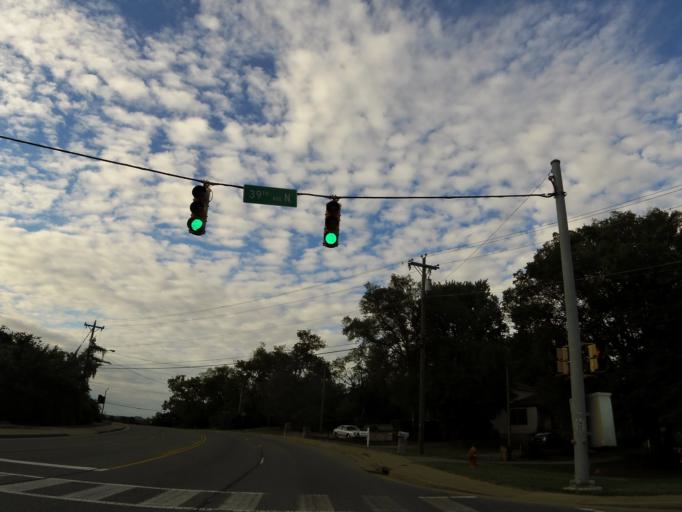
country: US
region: Tennessee
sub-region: Davidson County
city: Nashville
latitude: 36.1660
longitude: -86.8350
